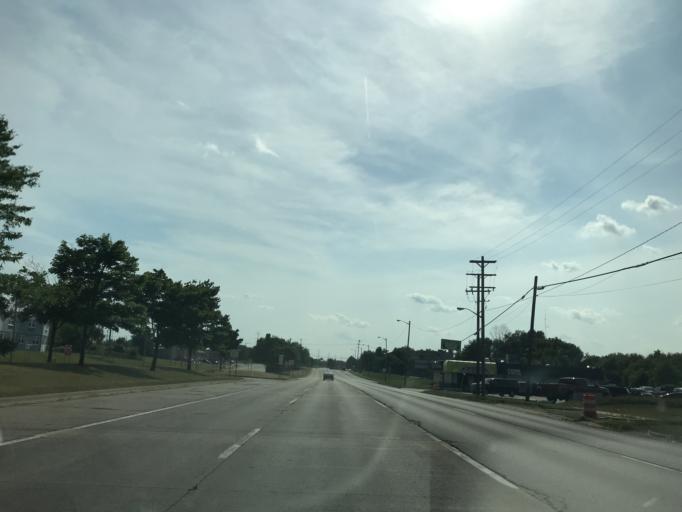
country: US
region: Michigan
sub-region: Wayne County
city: Inkster
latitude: 42.2883
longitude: -83.3348
